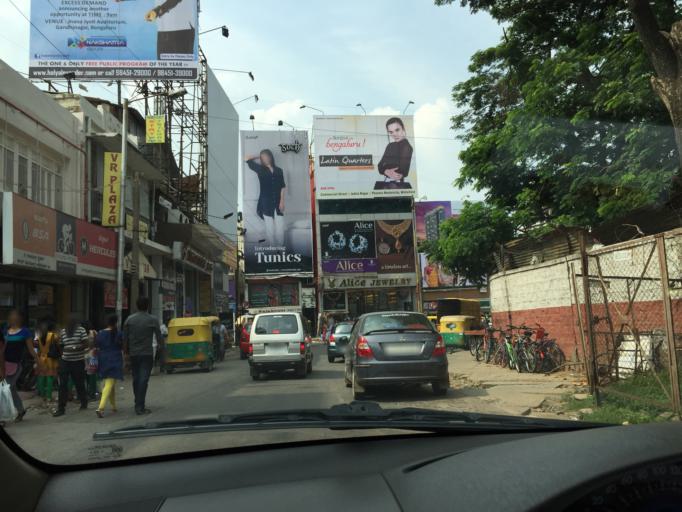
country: IN
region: Karnataka
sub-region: Bangalore Urban
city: Bangalore
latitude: 12.9813
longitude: 77.6079
